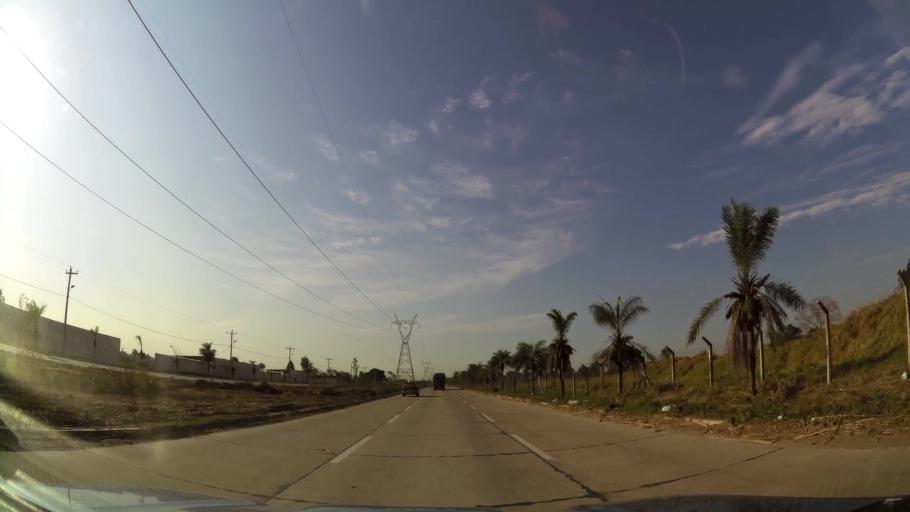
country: BO
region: Santa Cruz
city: Santa Cruz de la Sierra
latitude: -17.6977
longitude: -63.1355
